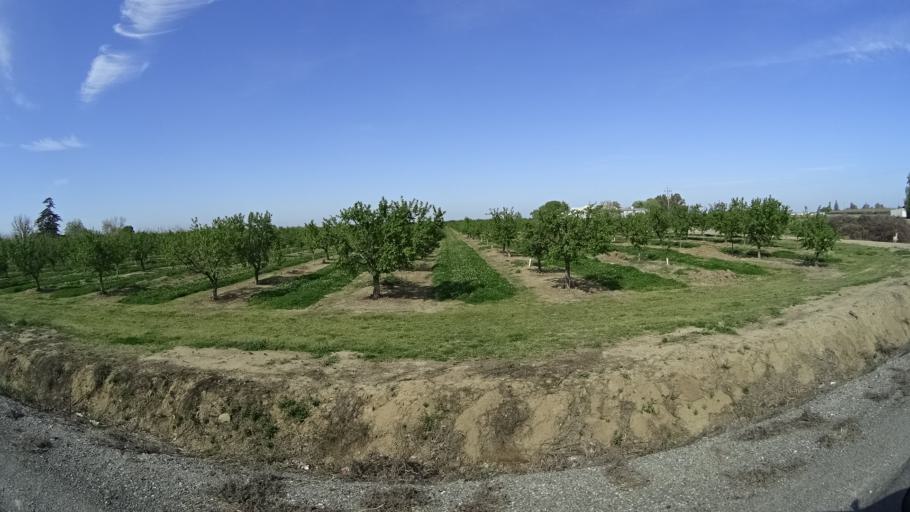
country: US
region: California
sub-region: Glenn County
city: Hamilton City
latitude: 39.6497
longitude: -122.0077
